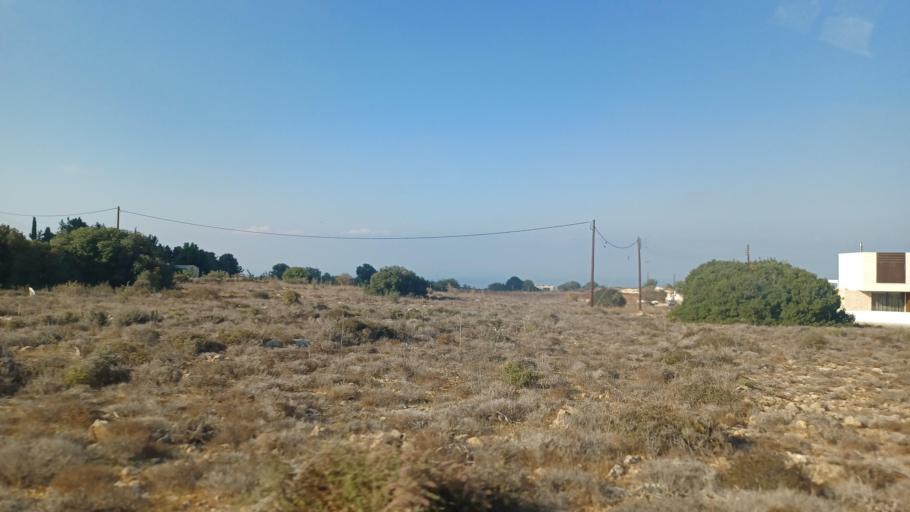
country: CY
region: Pafos
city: Mesogi
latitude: 34.7790
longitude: 32.4677
